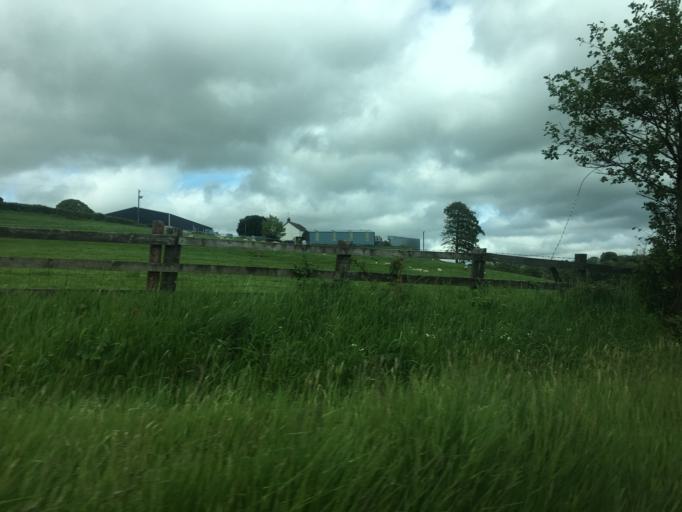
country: GB
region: Wales
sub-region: Carmarthenshire
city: Llansawel
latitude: 52.0729
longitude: -3.9979
